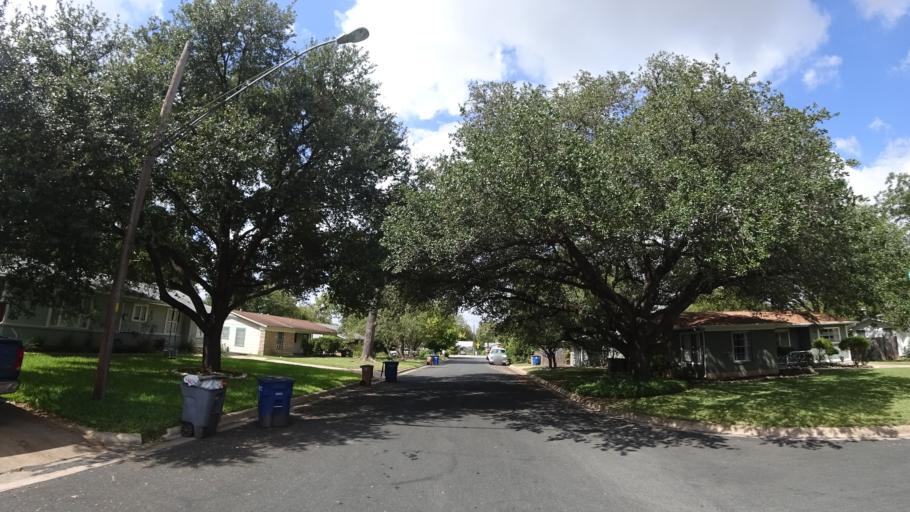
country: US
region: Texas
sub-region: Travis County
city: Austin
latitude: 30.3564
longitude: -97.7202
